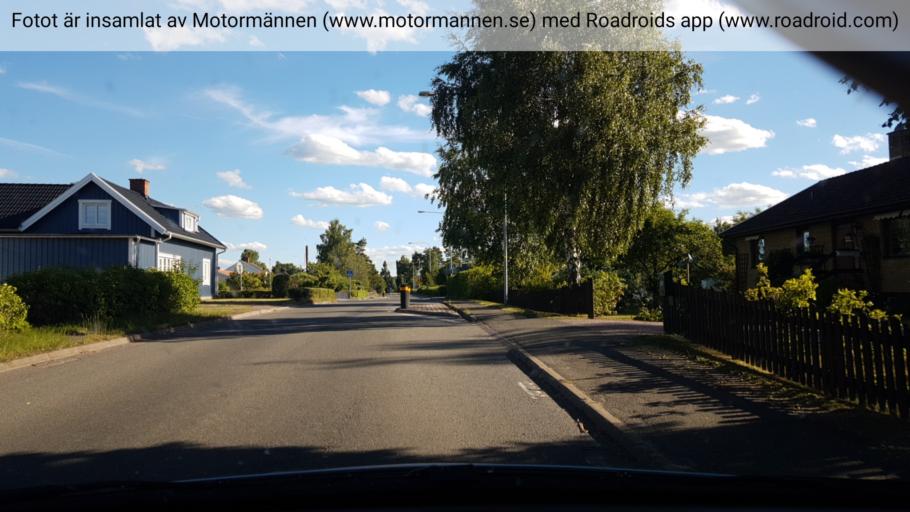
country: SE
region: Vaestra Goetaland
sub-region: Skovde Kommun
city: Stopen
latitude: 58.4800
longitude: 13.8658
